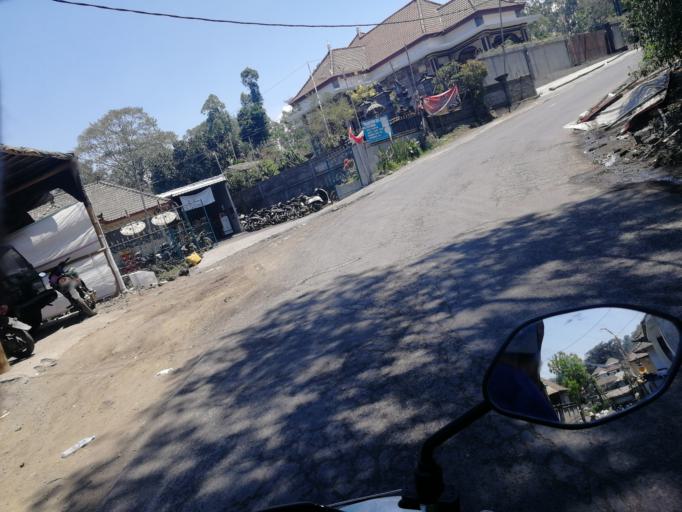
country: ID
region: Bali
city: Banjar Trunyan
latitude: -8.2293
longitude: 115.4093
